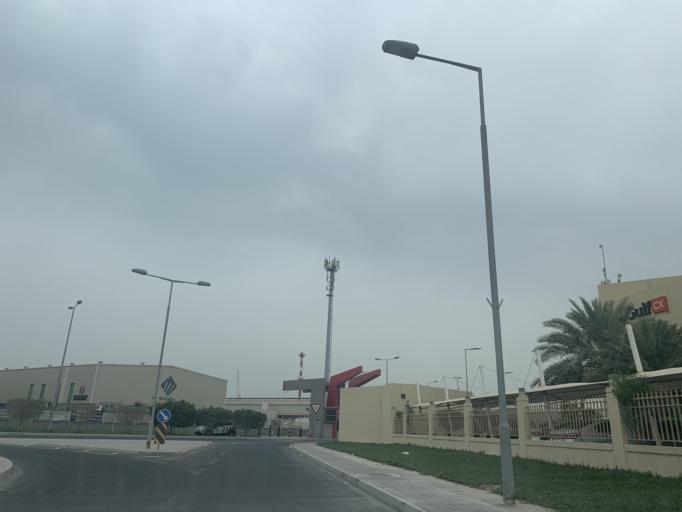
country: BH
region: Muharraq
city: Al Hadd
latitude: 26.2134
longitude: 50.6682
